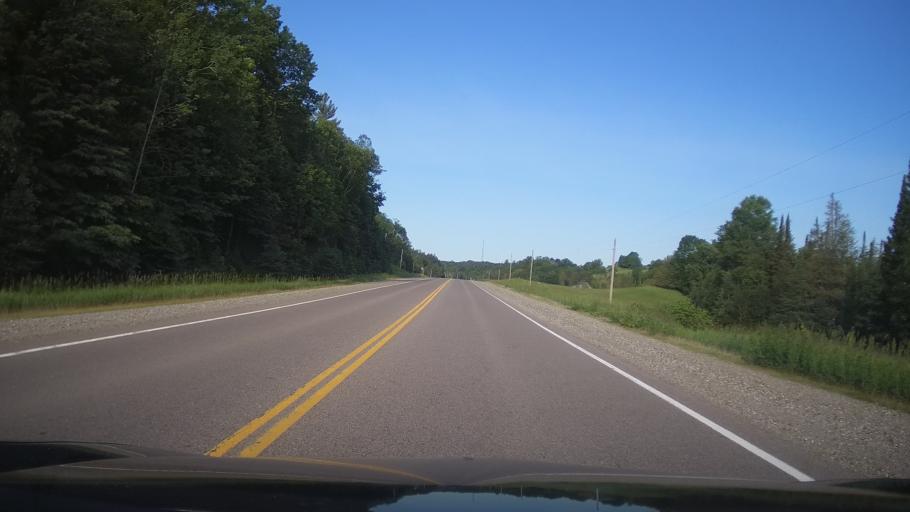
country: CA
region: Ontario
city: Skatepark
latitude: 44.7561
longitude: -76.8164
